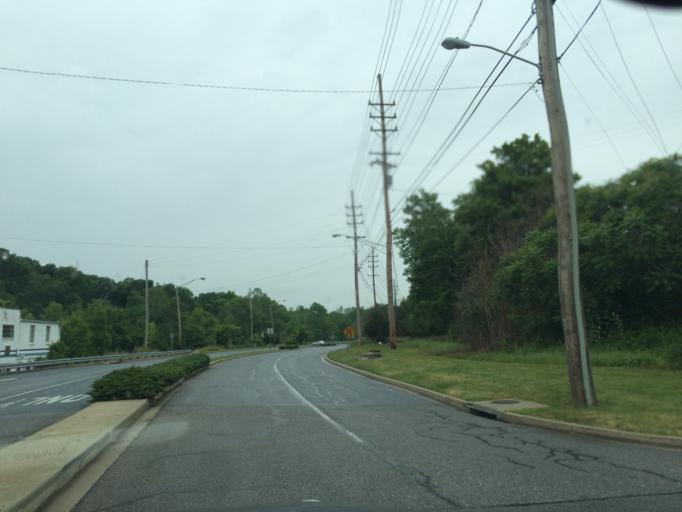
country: US
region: Maryland
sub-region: Washington County
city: Hagerstown
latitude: 39.6317
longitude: -77.7019
